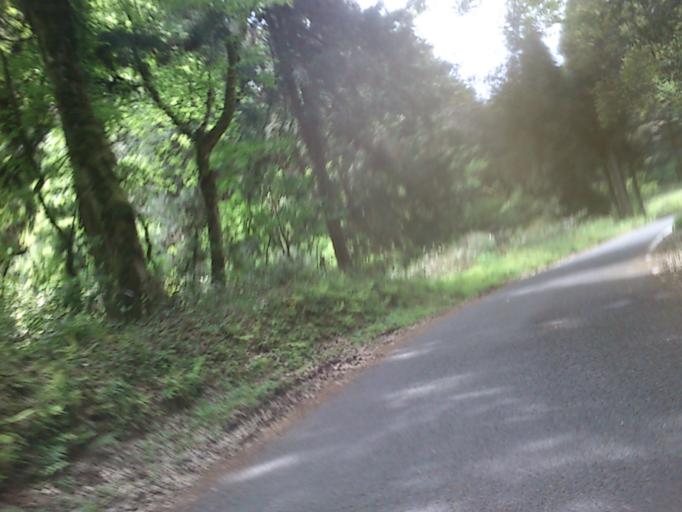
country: JP
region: Kyoto
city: Miyazu
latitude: 35.6115
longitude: 135.1131
